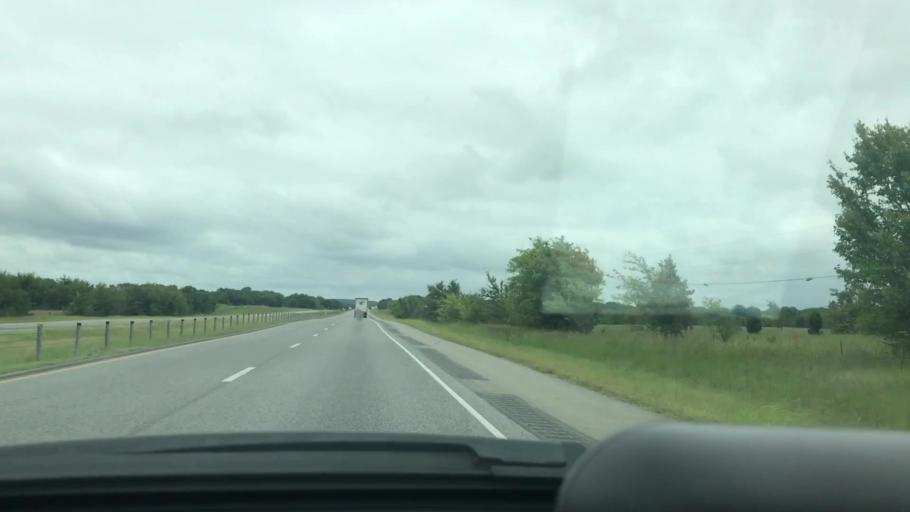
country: US
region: Oklahoma
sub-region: Pittsburg County
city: McAlester
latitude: 34.7558
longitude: -95.8924
